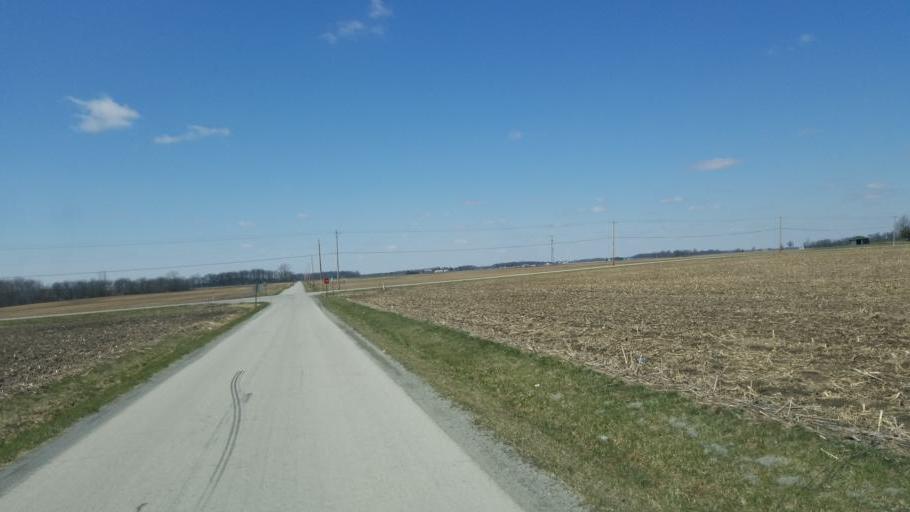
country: US
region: Ohio
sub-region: Wyandot County
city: Upper Sandusky
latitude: 40.7745
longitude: -83.2661
